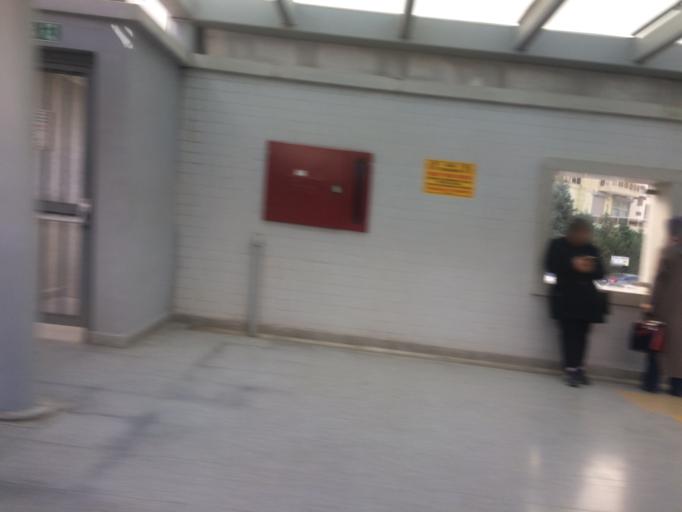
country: TR
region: Izmir
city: Karsiyaka
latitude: 38.4747
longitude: 27.0900
